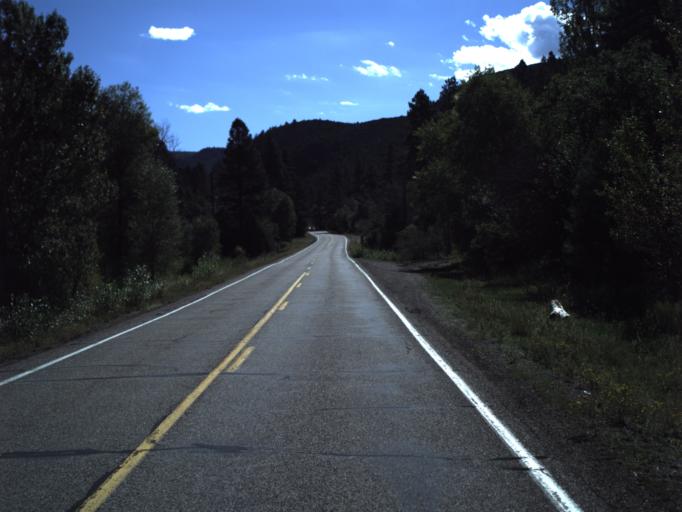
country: US
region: Utah
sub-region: Beaver County
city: Beaver
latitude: 38.2615
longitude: -112.5170
